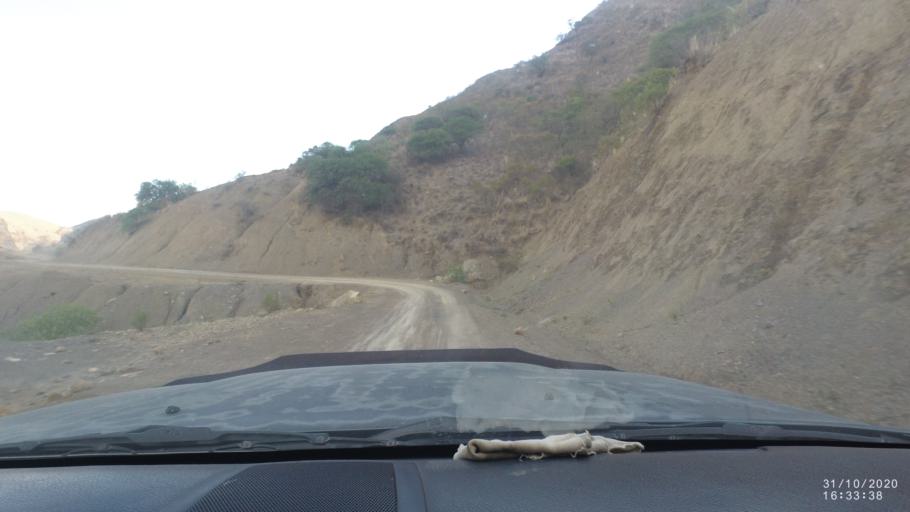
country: BO
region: Chuquisaca
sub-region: Provincia Zudanez
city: Mojocoya
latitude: -18.4435
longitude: -64.5848
